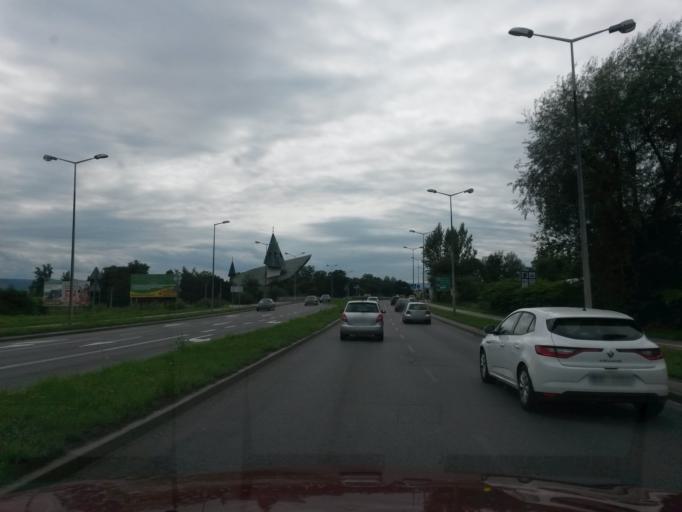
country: PL
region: Lesser Poland Voivodeship
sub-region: Powiat nowosadecki
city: Nowy Sacz
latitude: 49.6197
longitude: 20.7173
